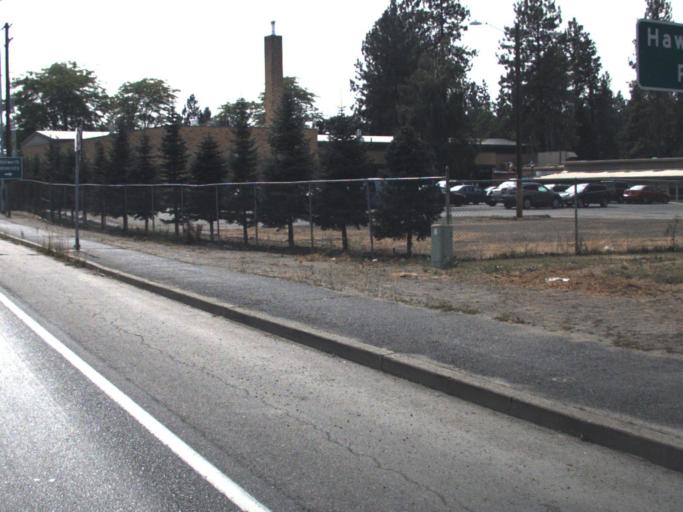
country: US
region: Washington
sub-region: Spokane County
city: Country Homes
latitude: 47.7523
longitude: -117.4105
